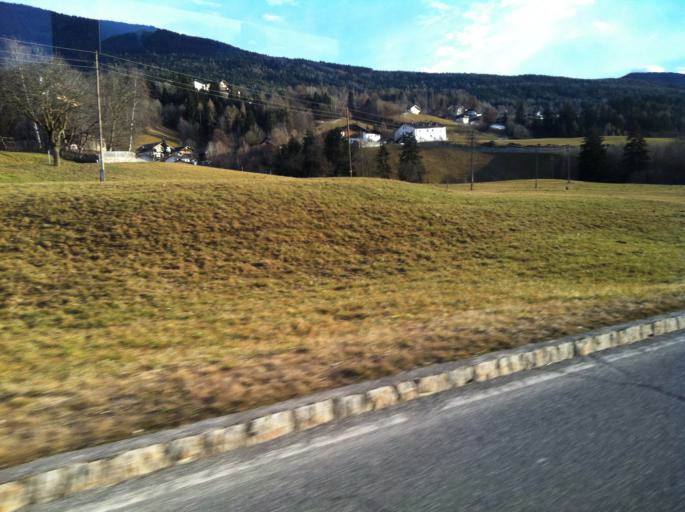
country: IT
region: Trentino-Alto Adige
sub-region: Bolzano
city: Bressanone
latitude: 46.6946
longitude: 11.6672
